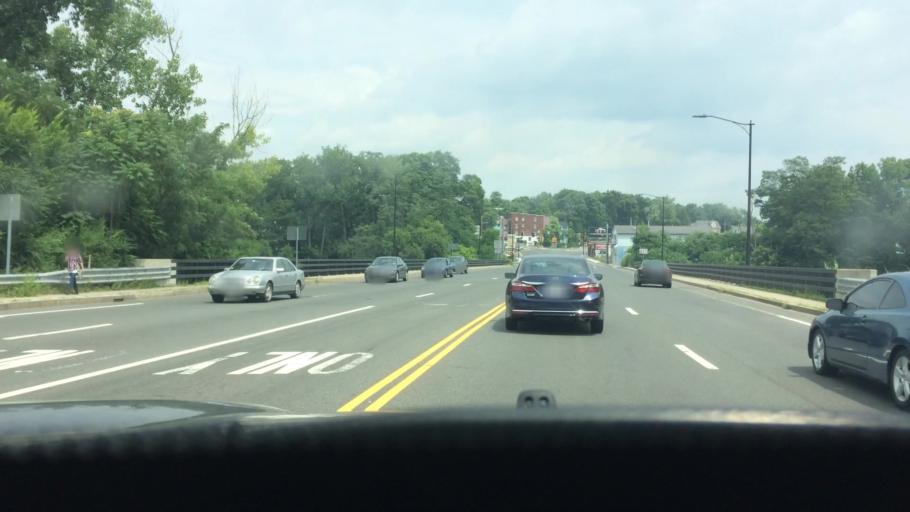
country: US
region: Massachusetts
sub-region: Hampden County
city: Chicopee
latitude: 42.1589
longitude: -72.5819
